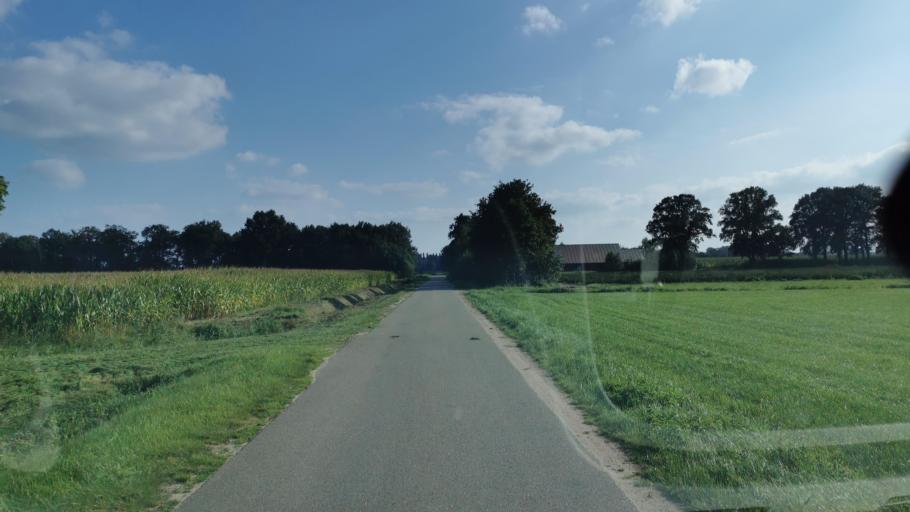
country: NL
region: Overijssel
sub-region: Gemeente Borne
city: Borne
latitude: 52.3395
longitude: 6.7640
